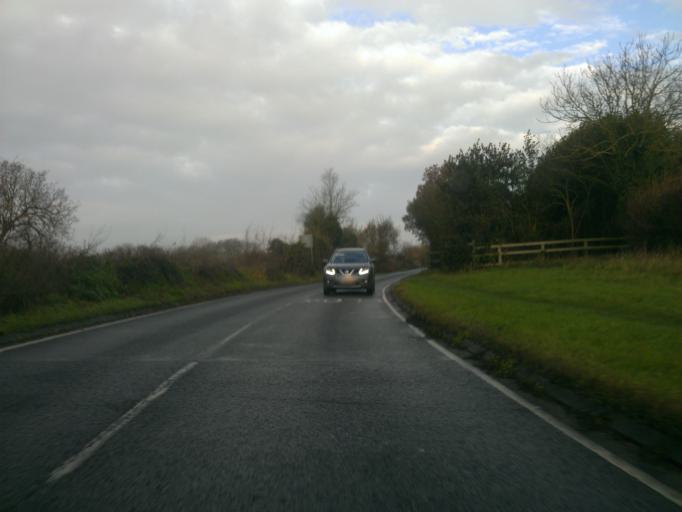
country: GB
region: England
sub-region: Essex
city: Wivenhoe
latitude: 51.8539
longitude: 0.9783
